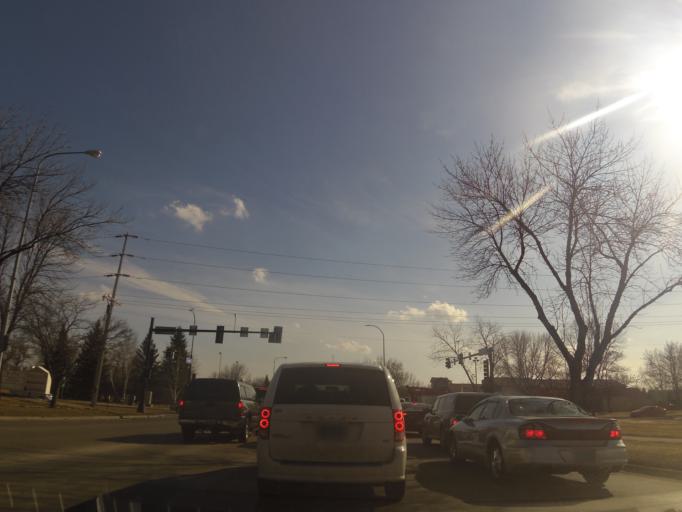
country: US
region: North Dakota
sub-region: Grand Forks County
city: Grand Forks
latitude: 47.9044
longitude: -97.0666
